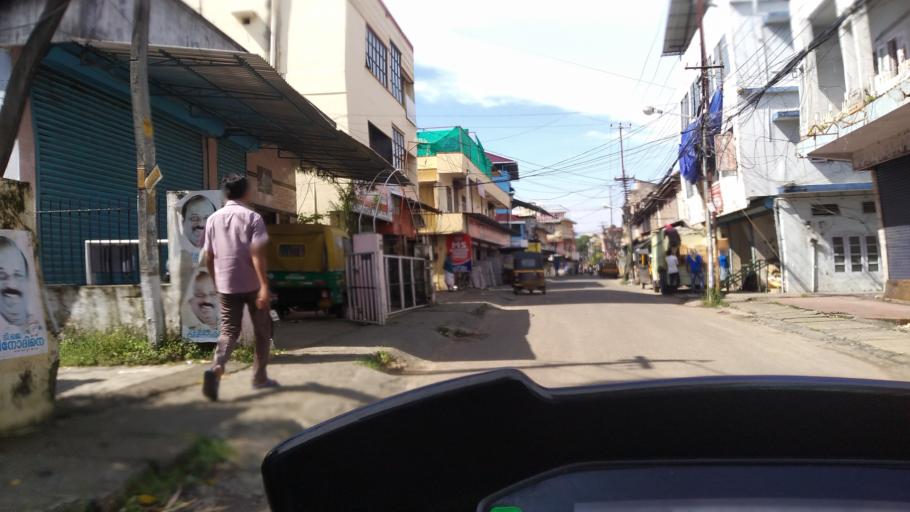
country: IN
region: Kerala
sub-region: Ernakulam
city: Cochin
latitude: 9.9773
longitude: 76.2816
